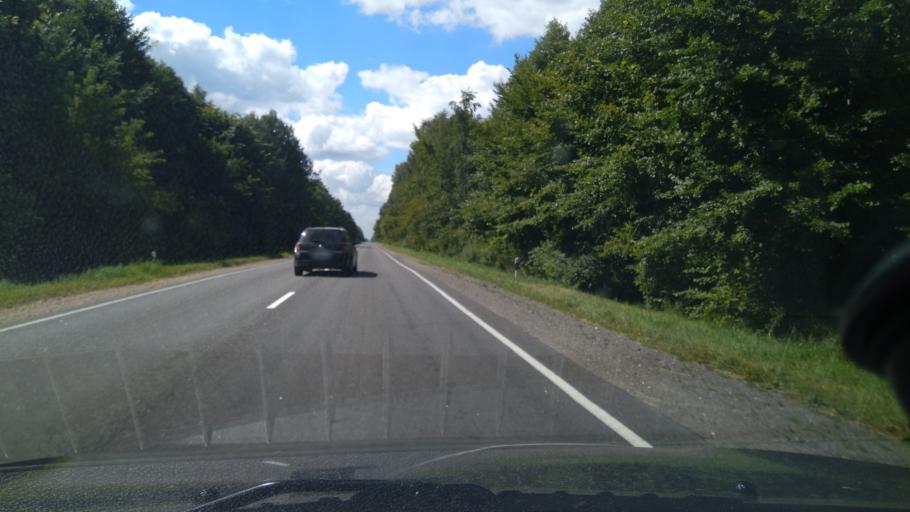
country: BY
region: Brest
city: Nyakhachava
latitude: 52.6657
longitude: 25.2494
